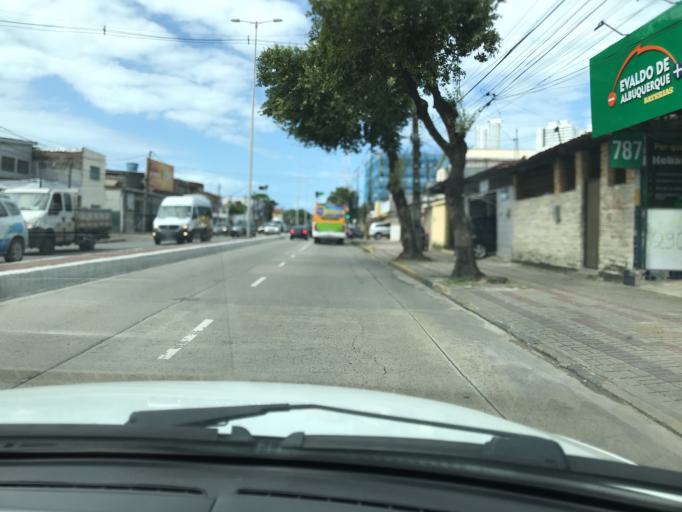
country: BR
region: Pernambuco
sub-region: Recife
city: Recife
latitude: -8.0453
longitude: -34.8799
